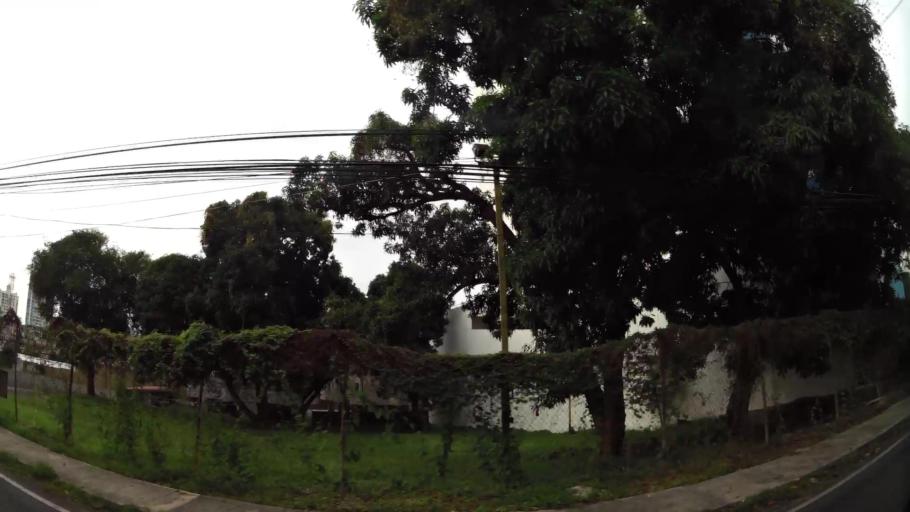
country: PA
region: Panama
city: Panama
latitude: 9.0024
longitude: -79.5125
